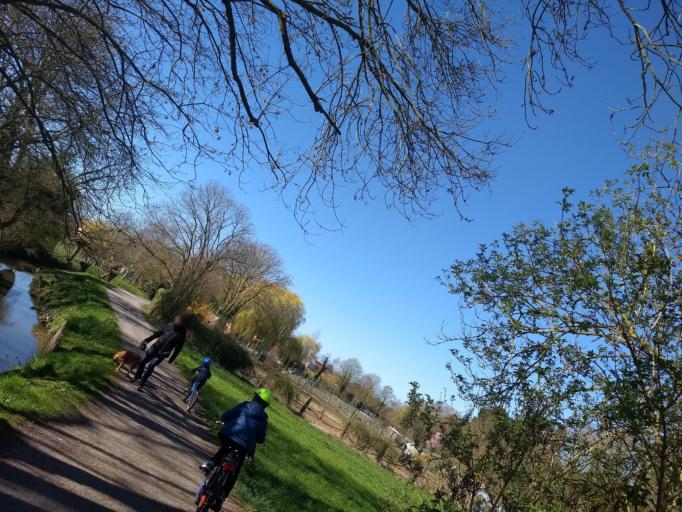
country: FR
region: Nord-Pas-de-Calais
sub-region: Departement du Pas-de-Calais
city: Achicourt
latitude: 50.2668
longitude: 2.7577
